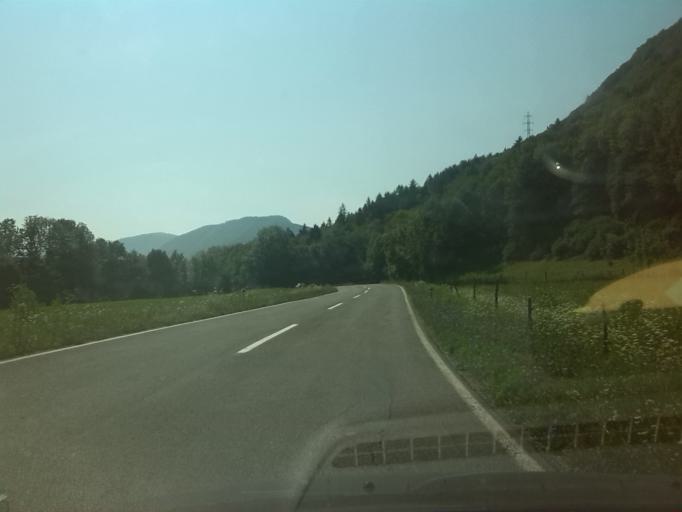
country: SI
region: Tolmin
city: Tolmin
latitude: 46.1916
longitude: 13.6984
